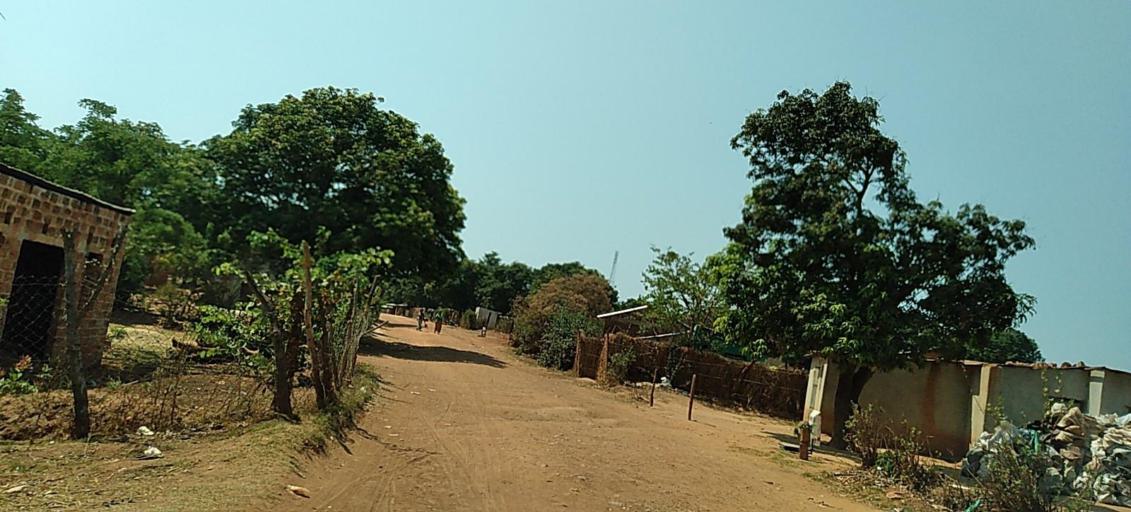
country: ZM
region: Copperbelt
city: Luanshya
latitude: -13.3531
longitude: 28.4124
